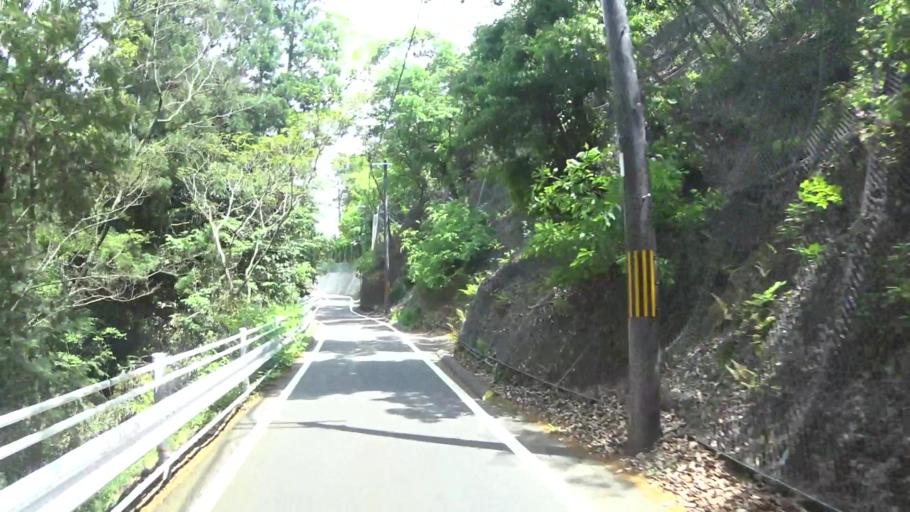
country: JP
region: Kyoto
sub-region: Kyoto-shi
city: Kamigyo-ku
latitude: 35.0579
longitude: 135.7285
